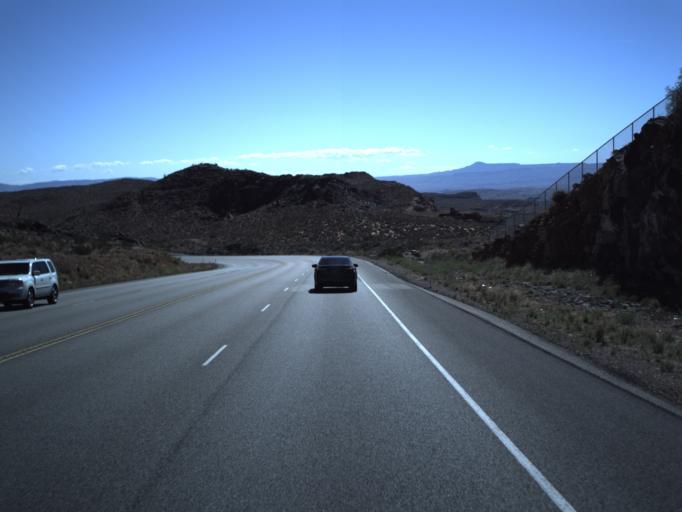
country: US
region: Utah
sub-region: Washington County
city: Santa Clara
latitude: 37.1631
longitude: -113.6110
